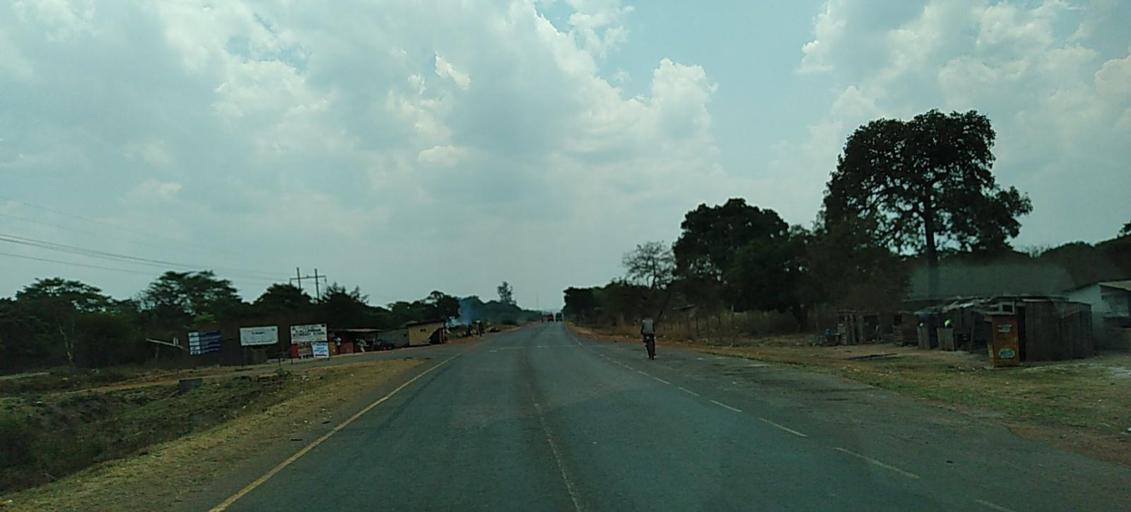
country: ZM
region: Copperbelt
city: Kalulushi
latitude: -12.8444
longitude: 28.0139
